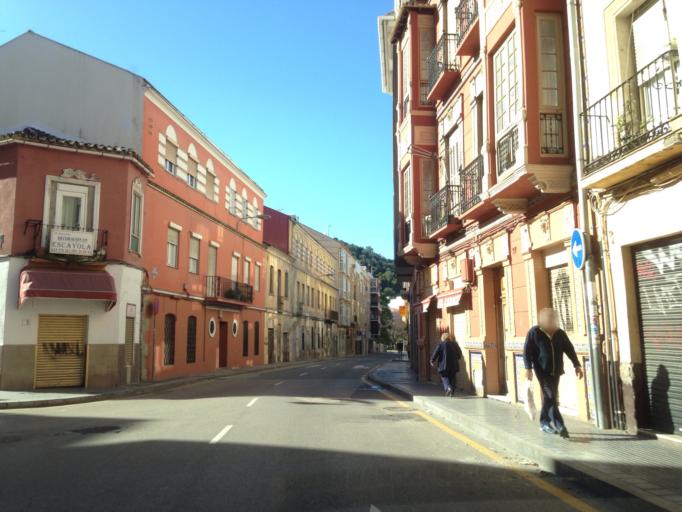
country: ES
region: Andalusia
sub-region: Provincia de Malaga
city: Malaga
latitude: 36.7289
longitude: -4.4145
